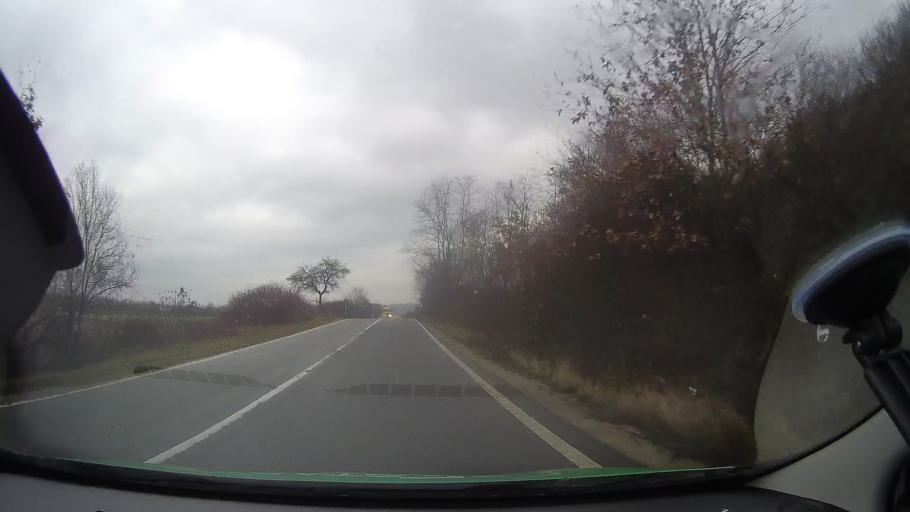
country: RO
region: Arad
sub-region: Comuna Almas
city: Almas
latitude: 46.2953
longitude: 22.2054
